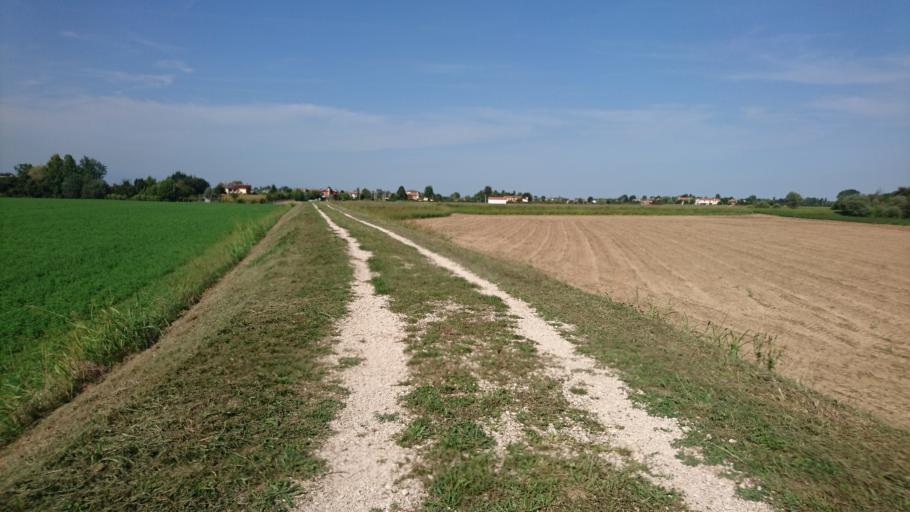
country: IT
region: Veneto
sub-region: Provincia di Padova
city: Saccolongo
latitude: 45.4208
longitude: 11.7302
